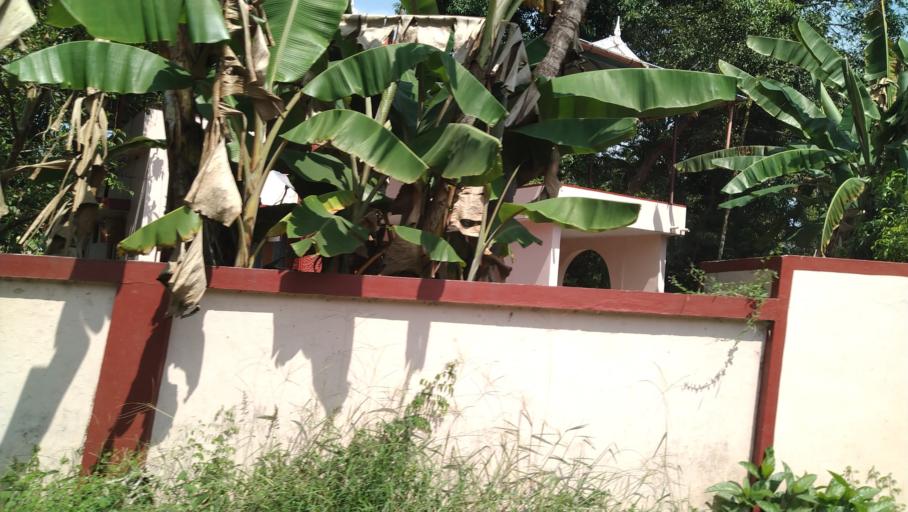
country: IN
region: Kerala
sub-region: Ernakulam
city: Aluva
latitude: 10.1257
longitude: 76.3520
